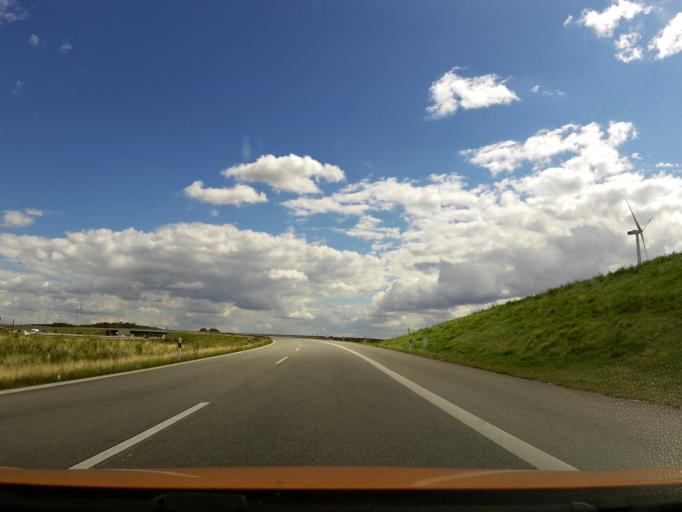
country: DE
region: Berlin
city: Falkenberg
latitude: 52.6148
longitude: 13.5422
